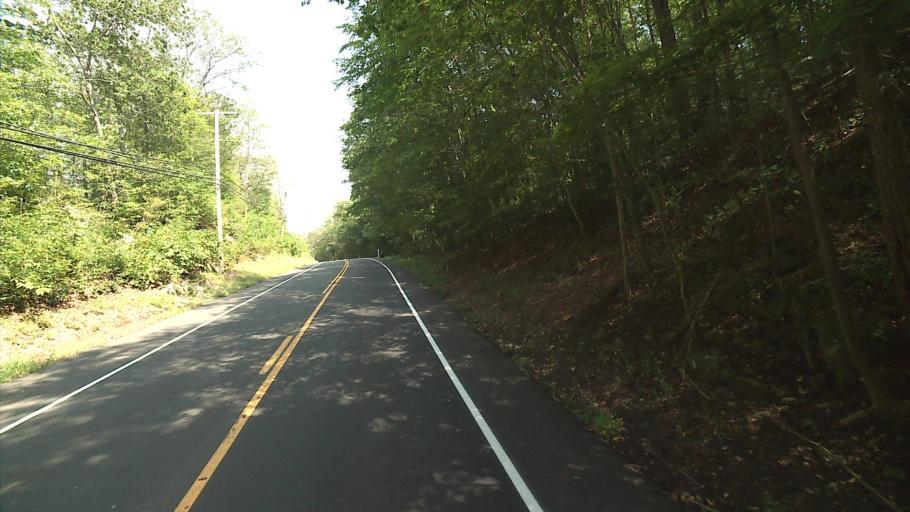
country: US
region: Connecticut
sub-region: Middlesex County
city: Durham
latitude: 41.4037
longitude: -72.6528
